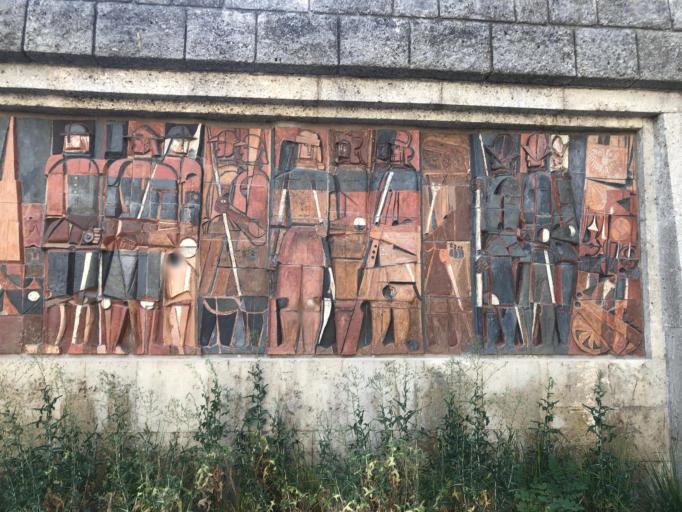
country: AT
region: Lower Austria
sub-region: Politischer Bezirk Korneuburg
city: Langenzersdorf
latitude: 48.2752
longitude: 16.3362
